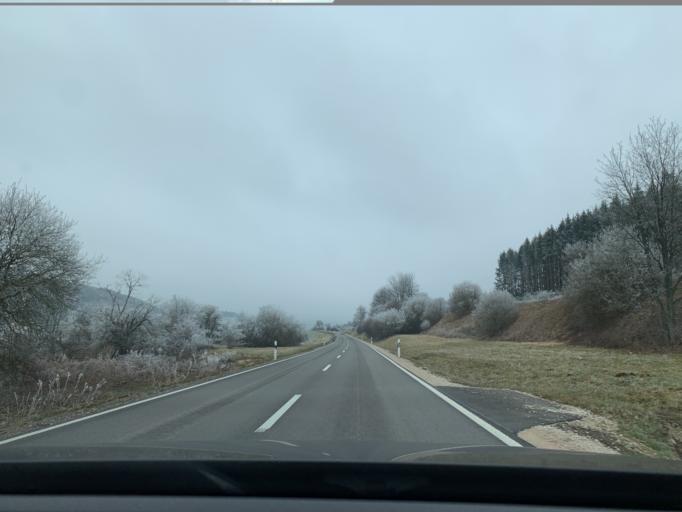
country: DE
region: Baden-Wuerttemberg
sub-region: Freiburg Region
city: Geisingen
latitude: 47.8933
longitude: 8.6658
